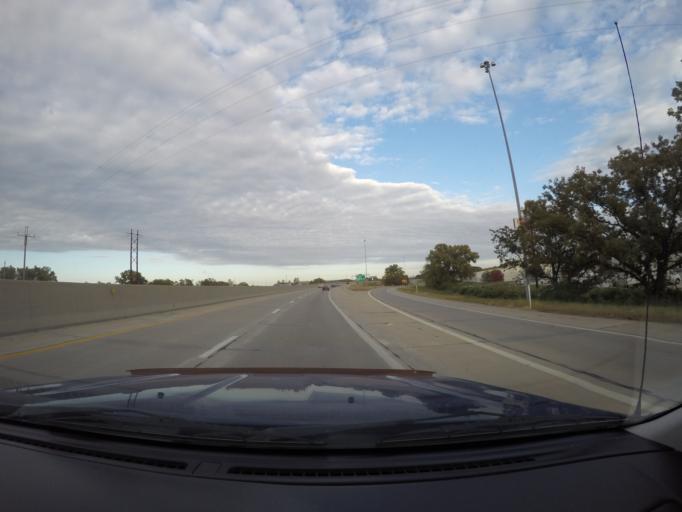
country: US
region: Kansas
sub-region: Shawnee County
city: Topeka
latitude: 39.0702
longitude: -95.7098
